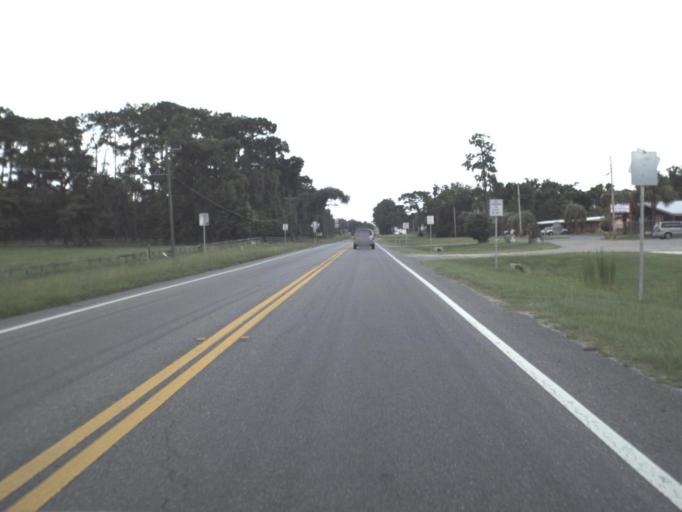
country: US
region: Florida
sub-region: Columbia County
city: Lake City
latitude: 30.1408
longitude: -82.6343
